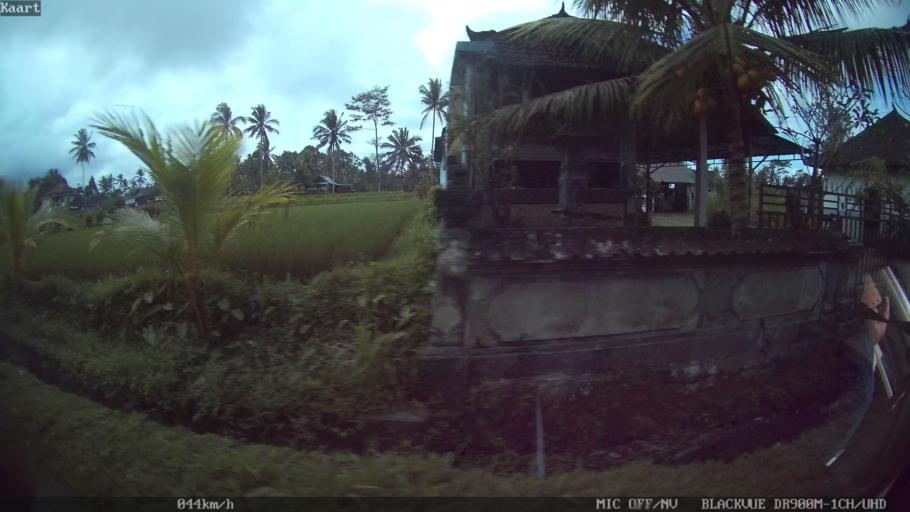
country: ID
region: Bali
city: Banjar Bebalang
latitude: -8.4660
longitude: 115.3833
